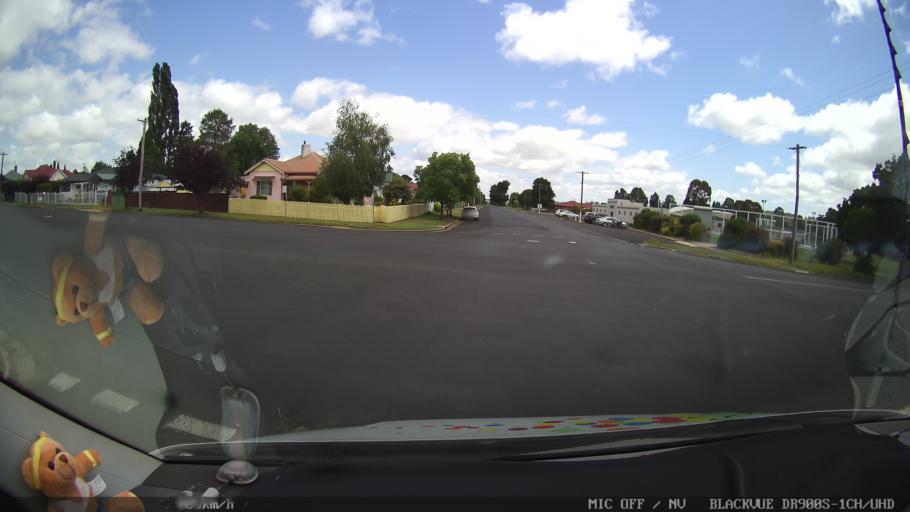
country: AU
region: New South Wales
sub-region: Glen Innes Severn
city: Glen Innes
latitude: -29.7330
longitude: 151.7332
